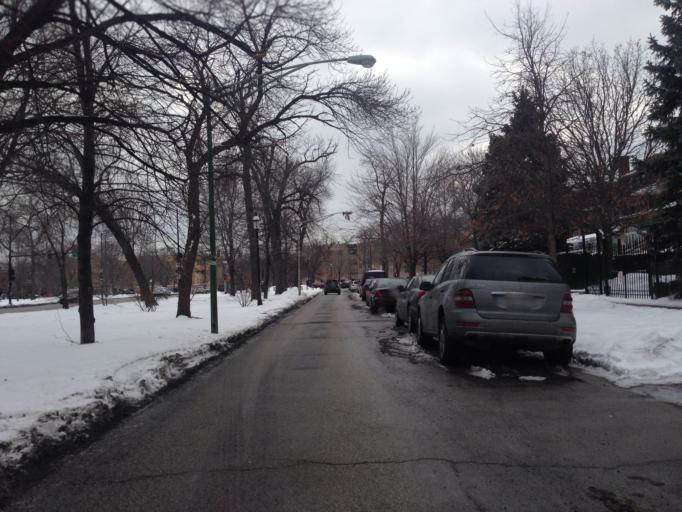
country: US
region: Illinois
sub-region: Cook County
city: Lincolnwood
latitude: 41.9224
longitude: -87.7075
